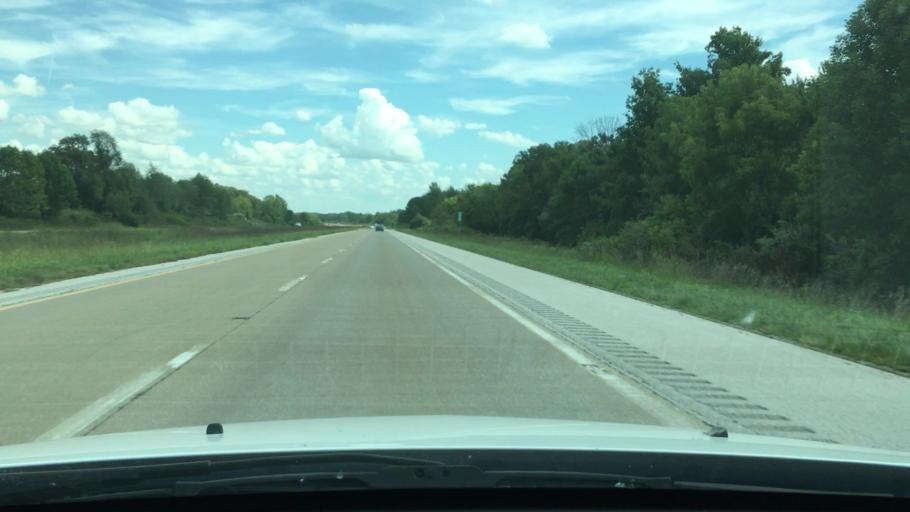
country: US
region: Illinois
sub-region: Scott County
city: Winchester
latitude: 39.6828
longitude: -90.5322
